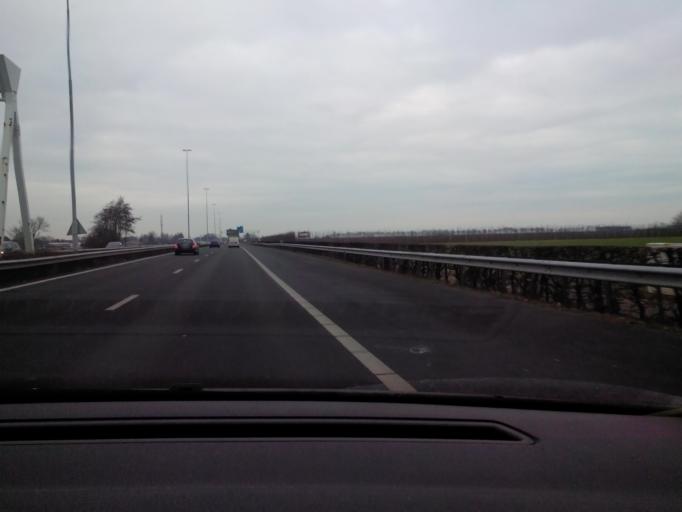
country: NL
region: North Brabant
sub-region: Gemeente Woudrichem
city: Almkerk
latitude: 51.7625
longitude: 4.9274
